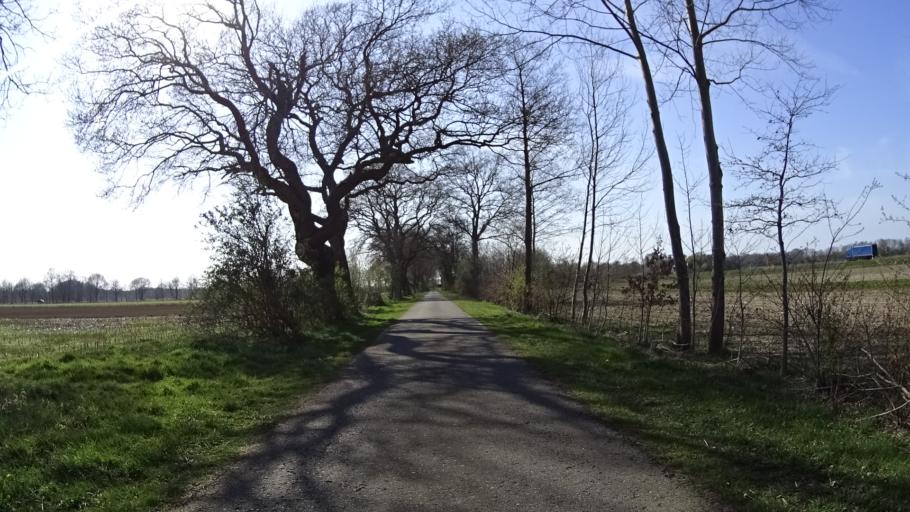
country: DE
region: Lower Saxony
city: Dorpen
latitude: 52.9776
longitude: 7.3131
